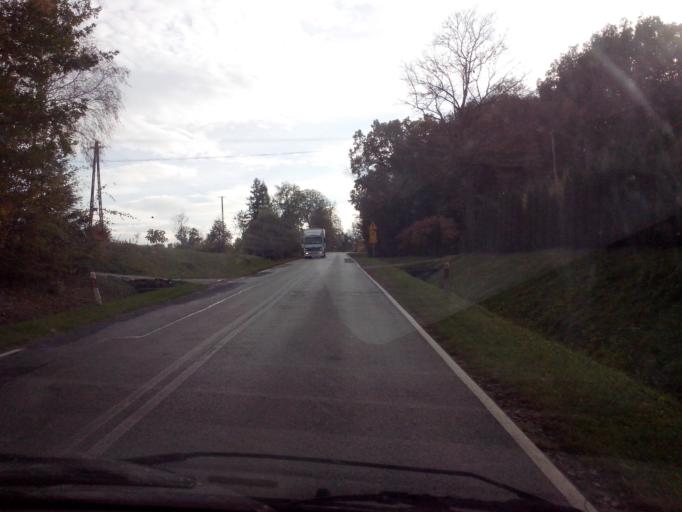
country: PL
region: Subcarpathian Voivodeship
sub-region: Powiat ropczycko-sedziszowski
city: Wielopole Skrzynskie
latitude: 49.9378
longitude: 21.6164
